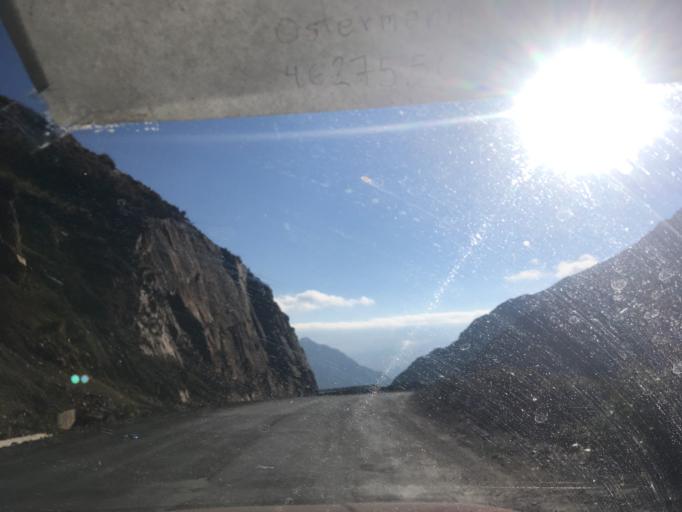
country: BO
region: La Paz
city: Quime
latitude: -17.0132
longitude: -67.2761
